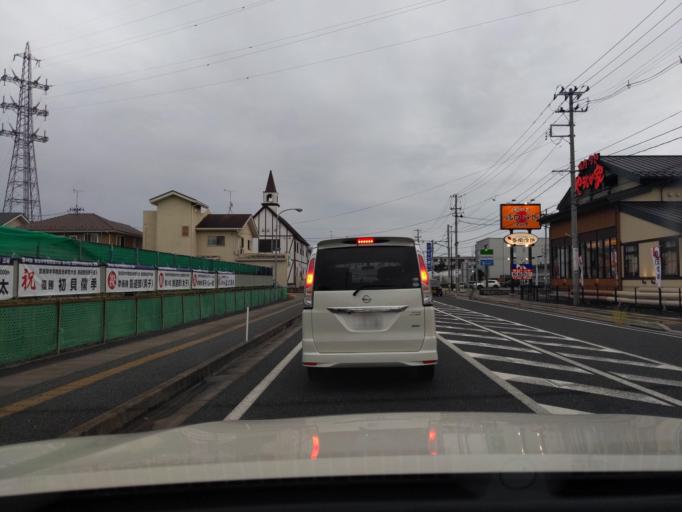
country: JP
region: Miyagi
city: Ishinomaki
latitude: 38.4459
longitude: 141.2634
